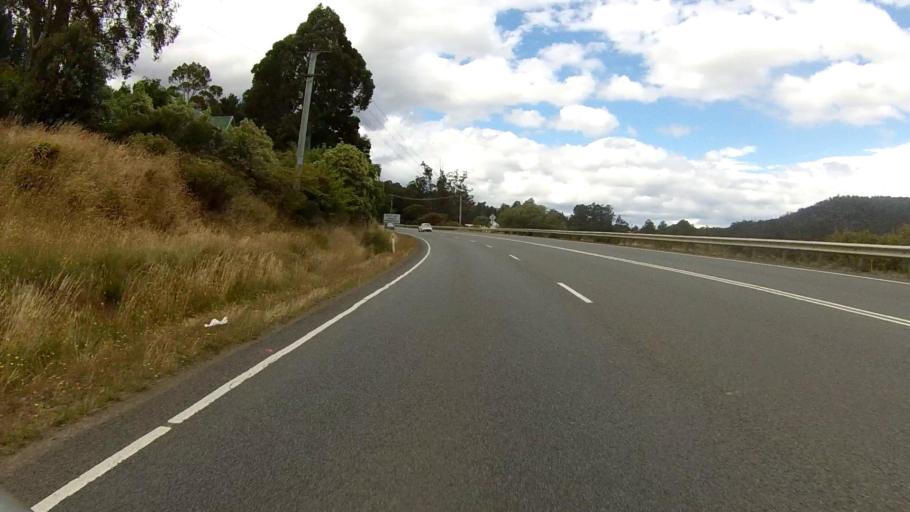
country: AU
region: Tasmania
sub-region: Huon Valley
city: Huonville
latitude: -42.9775
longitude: 147.1417
